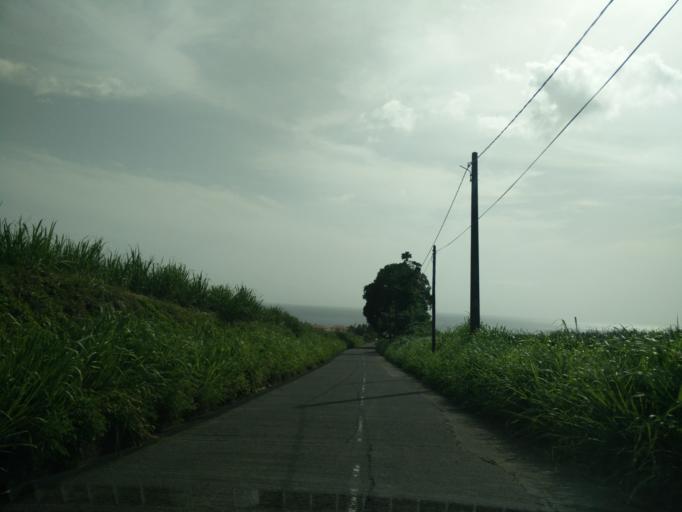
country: MQ
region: Martinique
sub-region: Martinique
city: Saint-Pierre
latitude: 14.7550
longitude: -61.1679
